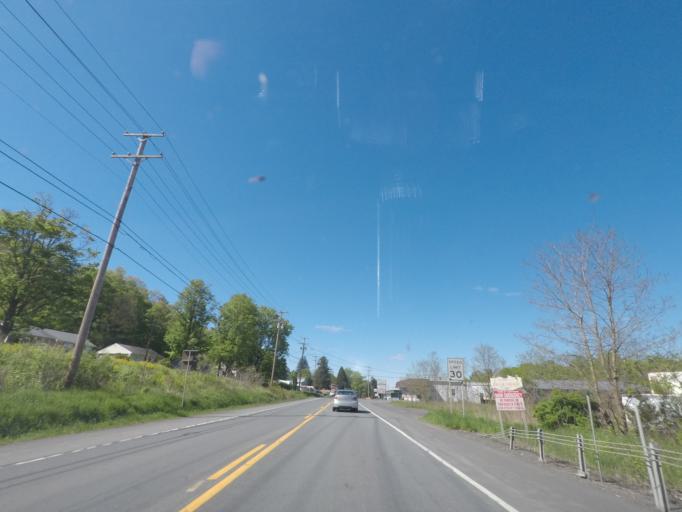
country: US
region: New York
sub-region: Albany County
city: Ravena
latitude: 42.4617
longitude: -73.8174
